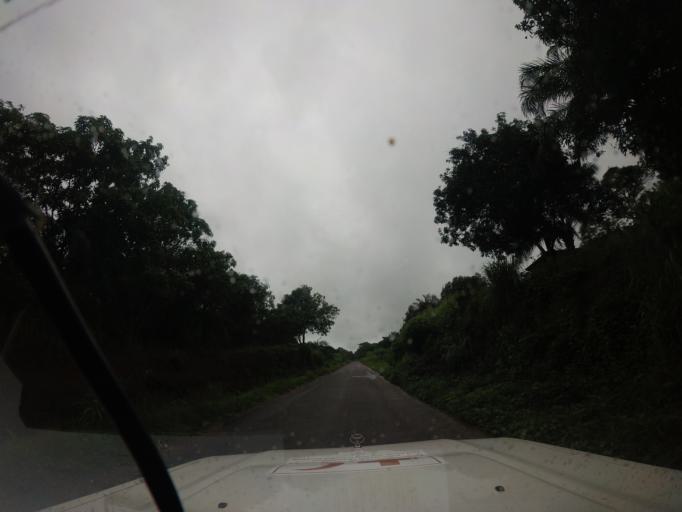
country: SL
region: Northern Province
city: Kabala
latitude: 9.3926
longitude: -11.7380
